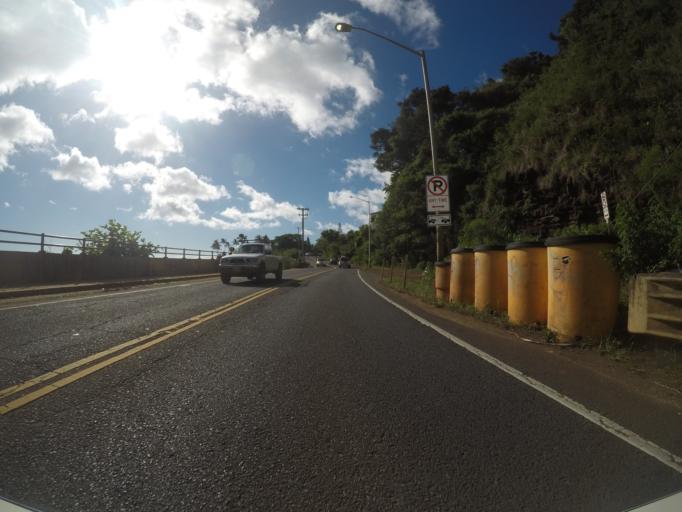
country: US
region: Hawaii
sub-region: Honolulu County
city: Pupukea
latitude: 21.6421
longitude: -158.0625
